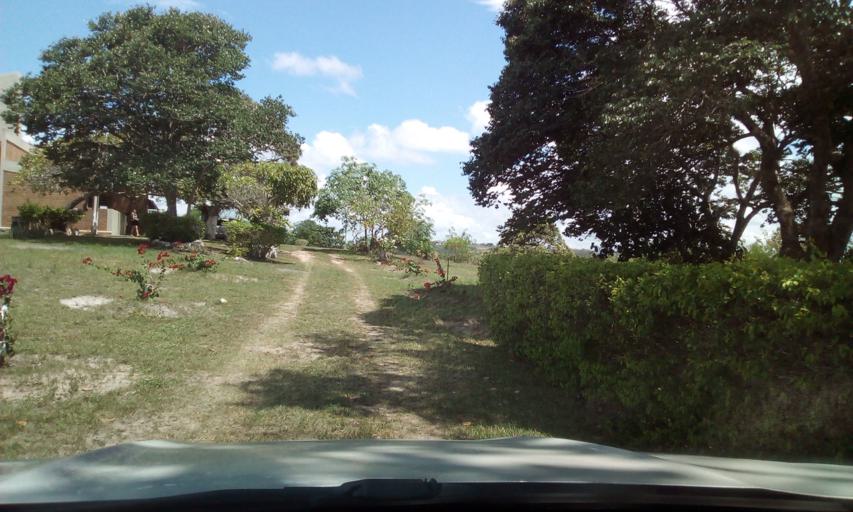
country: BR
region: Pernambuco
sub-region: Cha Grande
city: Cha Grande
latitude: -8.1958
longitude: -35.4951
